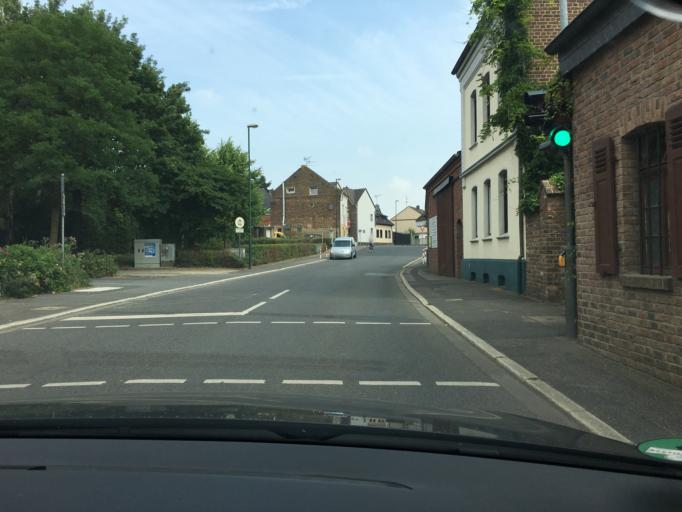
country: DE
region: North Rhine-Westphalia
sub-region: Regierungsbezirk Koln
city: Merzenich
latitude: 50.8570
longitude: 6.5860
